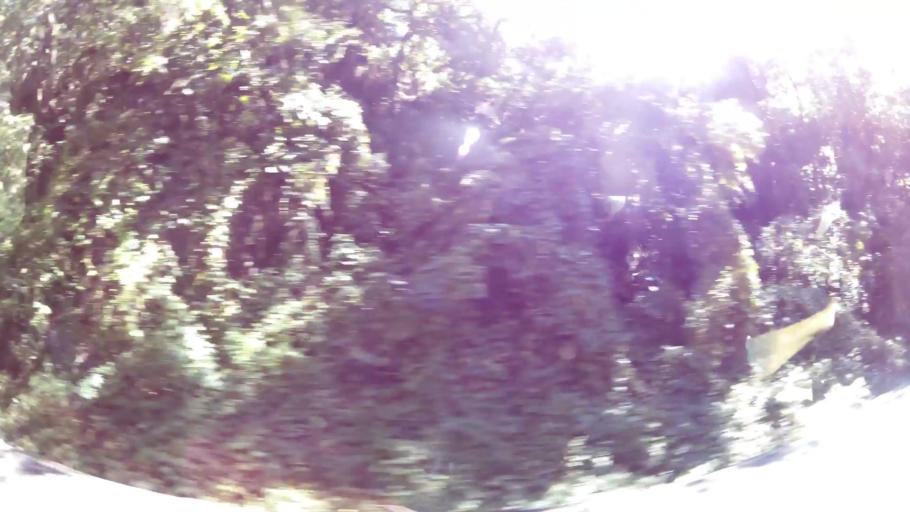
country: GT
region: Solola
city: Solola
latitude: 14.7586
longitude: -91.1751
